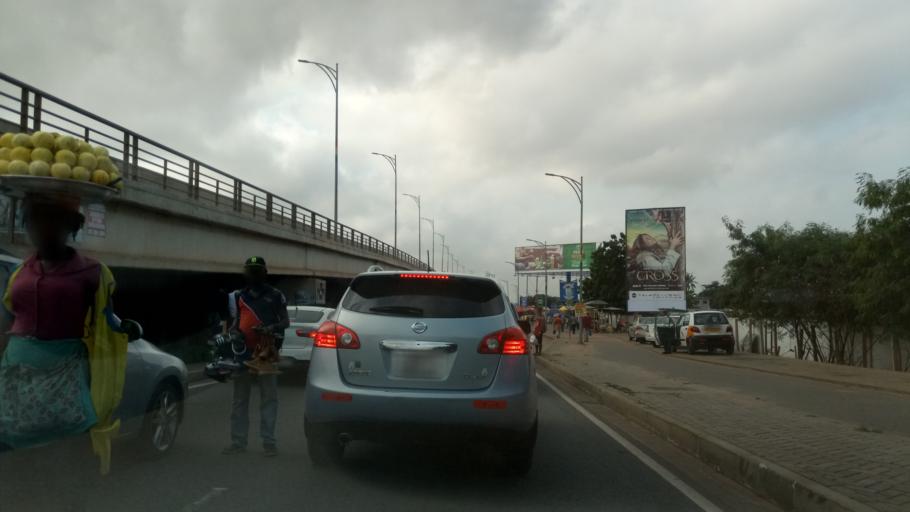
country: GH
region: Greater Accra
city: Medina Estates
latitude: 5.6654
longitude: -0.1773
